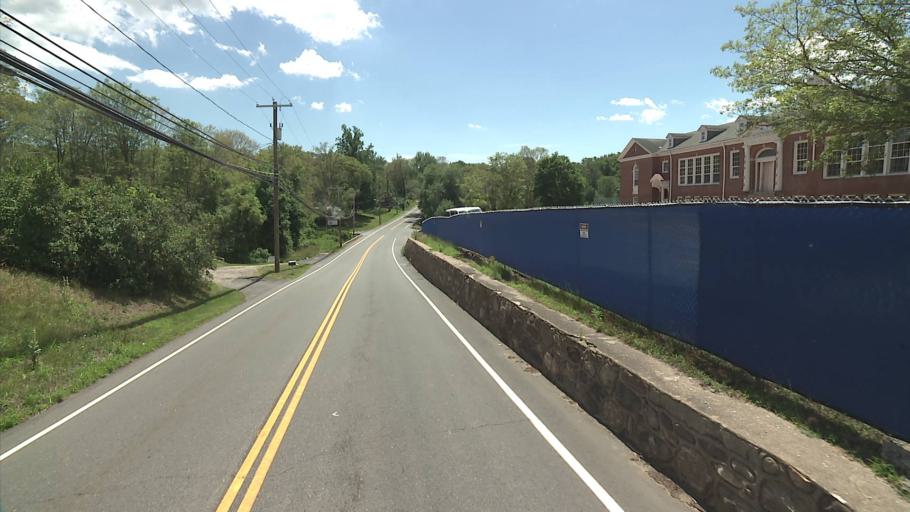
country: US
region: Connecticut
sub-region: Middlesex County
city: Moodus
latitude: 41.4990
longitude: -72.4494
